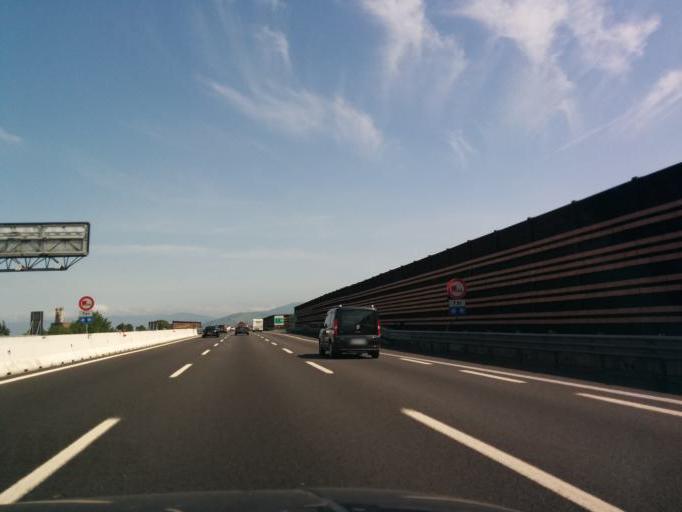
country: IT
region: Tuscany
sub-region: Province of Florence
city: Mantignano-Ugnano
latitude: 43.7822
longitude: 11.1601
